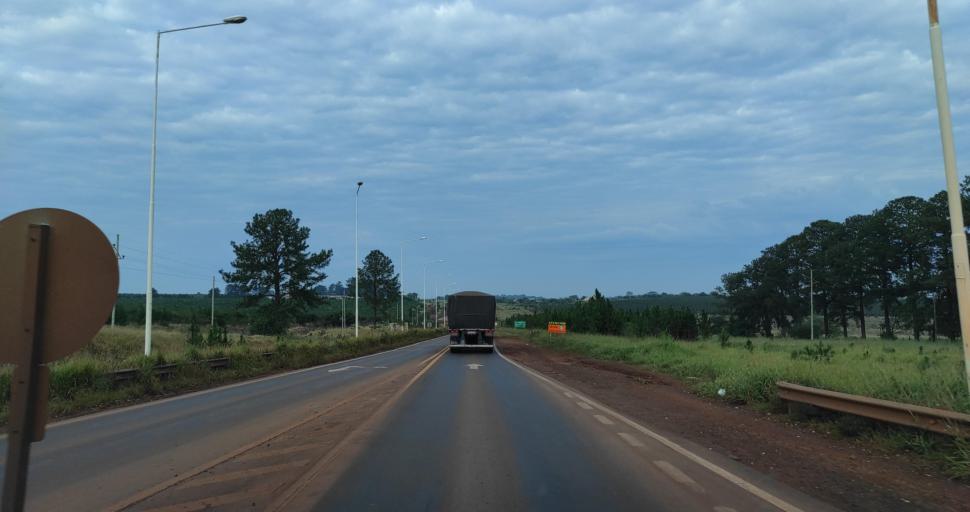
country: AR
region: Corrientes
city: Gobernador Ingeniero Valentin Virasoro
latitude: -27.9685
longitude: -56.0094
